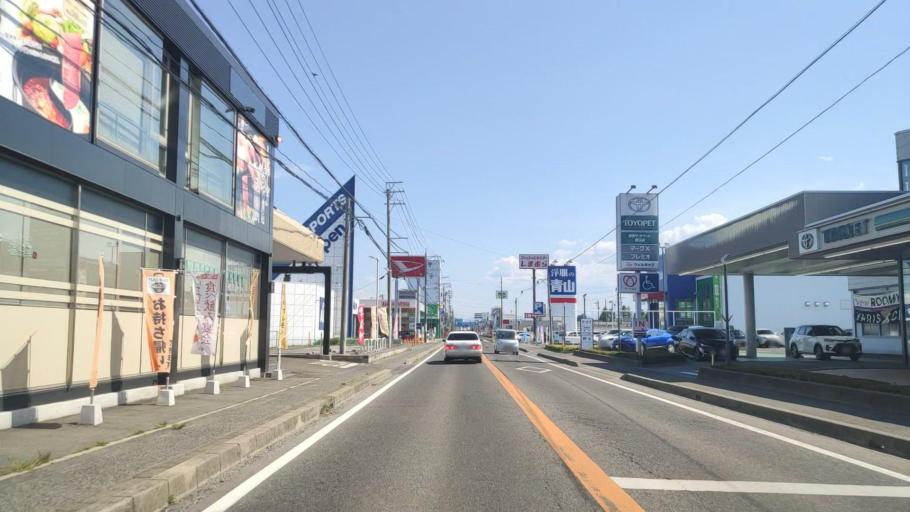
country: JP
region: Nagano
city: Hotaka
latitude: 36.3286
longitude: 137.8922
